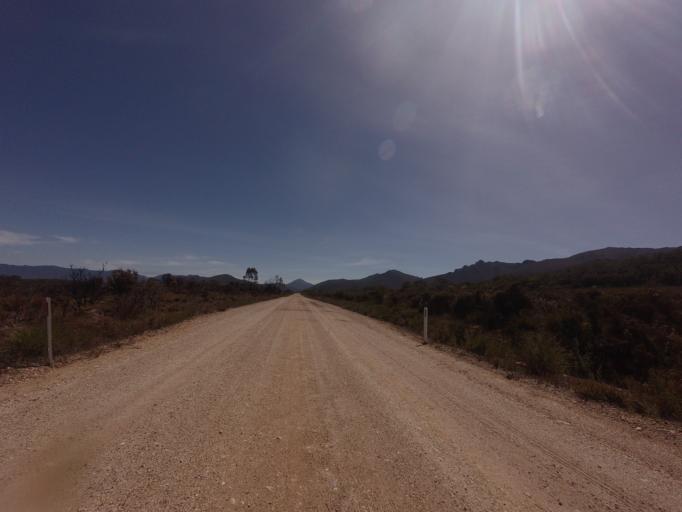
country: AU
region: Tasmania
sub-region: Huon Valley
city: Geeveston
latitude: -42.9712
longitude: 146.3642
